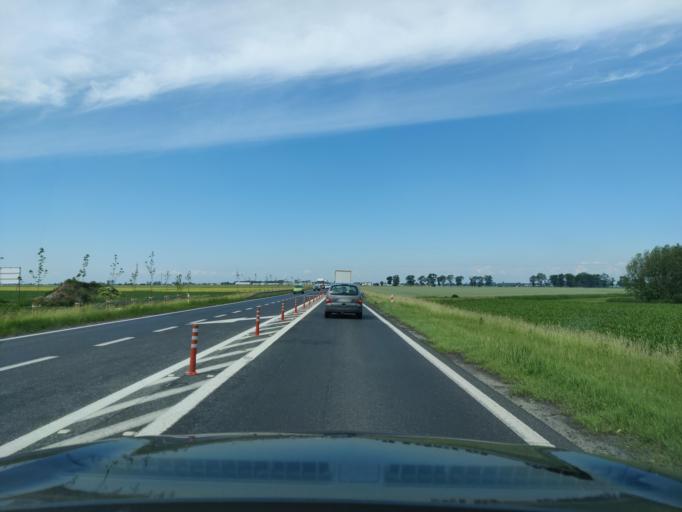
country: PL
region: Greater Poland Voivodeship
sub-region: Powiat grodziski
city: Granowo
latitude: 52.2215
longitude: 16.5659
